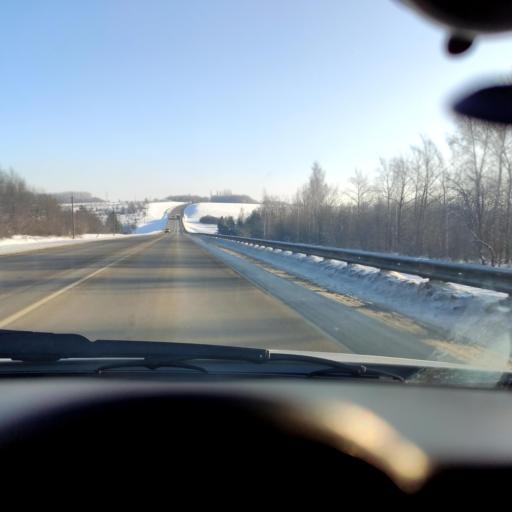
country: RU
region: Kursk
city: Shchigry
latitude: 51.6548
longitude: 36.8992
